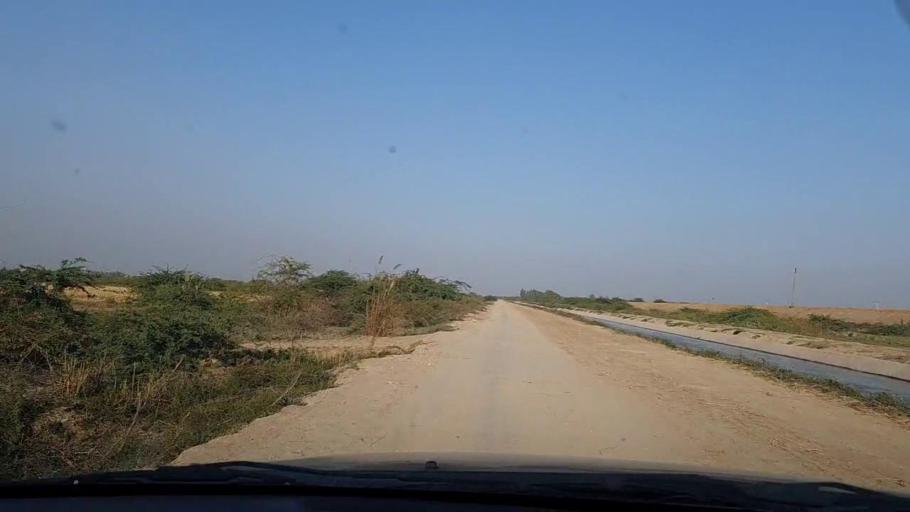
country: PK
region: Sindh
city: Chuhar Jamali
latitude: 24.2842
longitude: 67.7466
